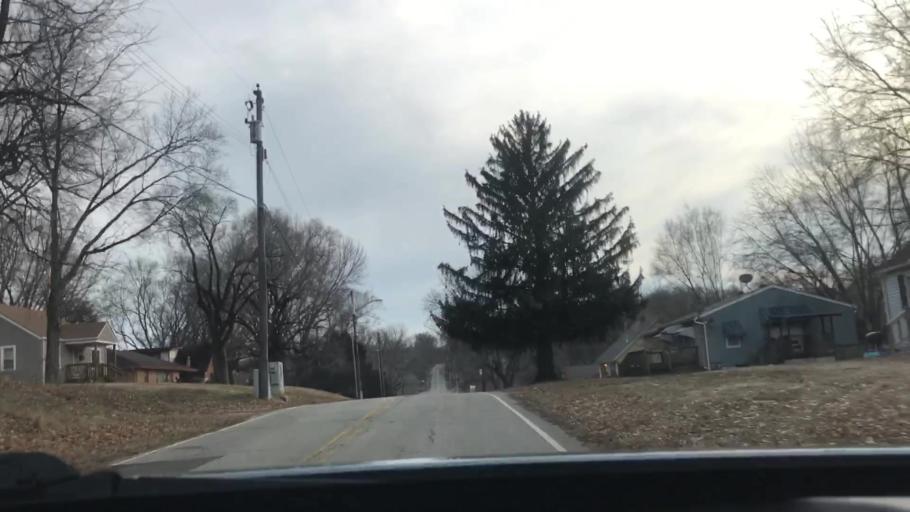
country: US
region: Missouri
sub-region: Jackson County
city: Independence
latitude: 39.0746
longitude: -94.4426
